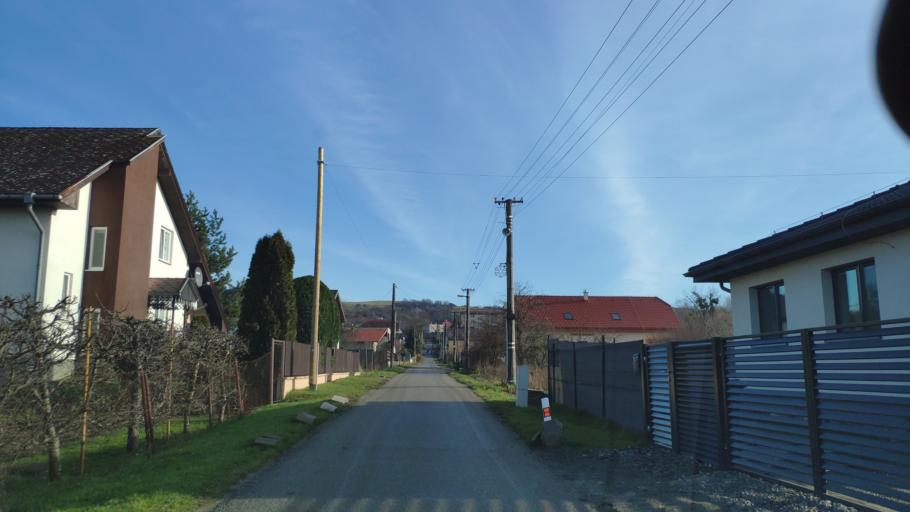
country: SK
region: Kosicky
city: Kosice
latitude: 48.6900
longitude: 21.3431
